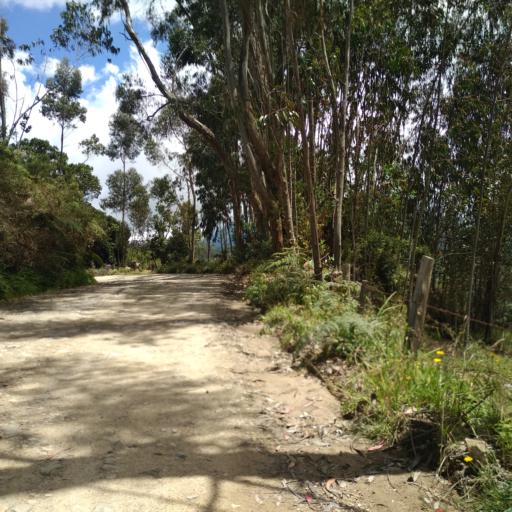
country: CO
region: Boyaca
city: Duitama
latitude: 5.9435
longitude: -73.1360
